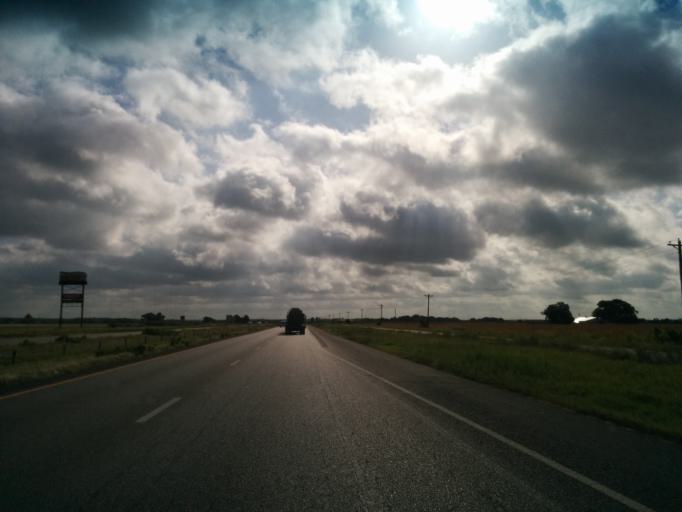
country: US
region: Texas
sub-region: Guadalupe County
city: Marion
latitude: 29.5203
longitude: -98.1352
